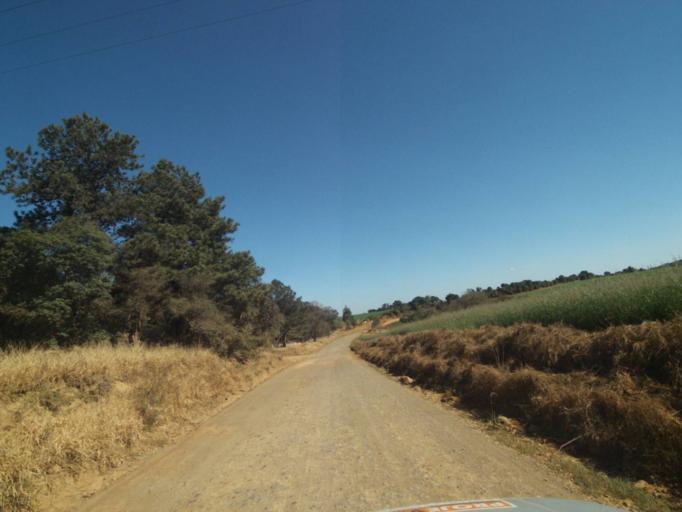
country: BR
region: Parana
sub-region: Reserva
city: Reserva
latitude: -24.6272
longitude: -50.6210
